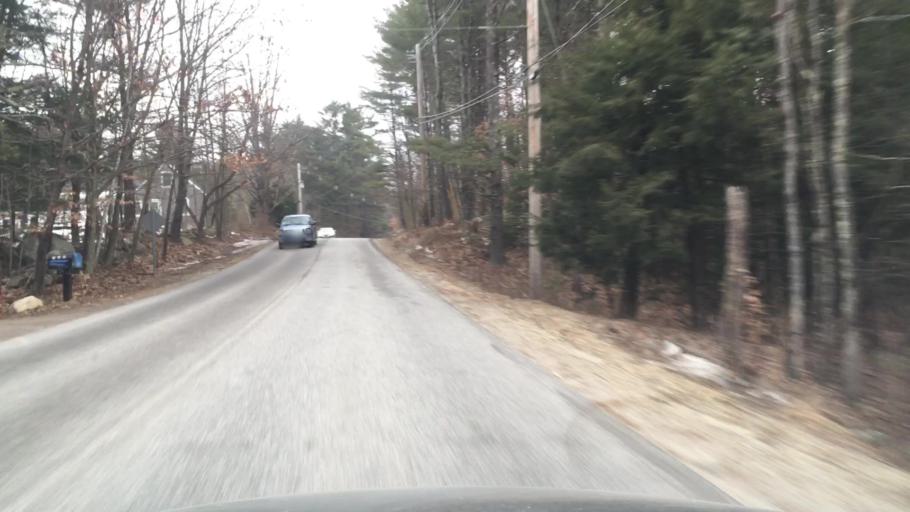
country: US
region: New Hampshire
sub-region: Hillsborough County
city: Goffstown
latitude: 42.9647
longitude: -71.6202
